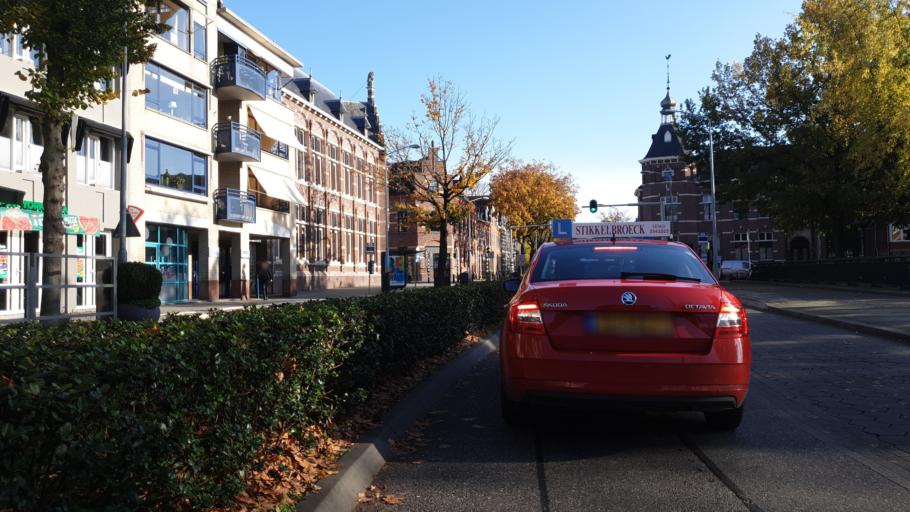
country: NL
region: Limburg
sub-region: Gemeente Venlo
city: Venlo
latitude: 51.3725
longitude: 6.1726
